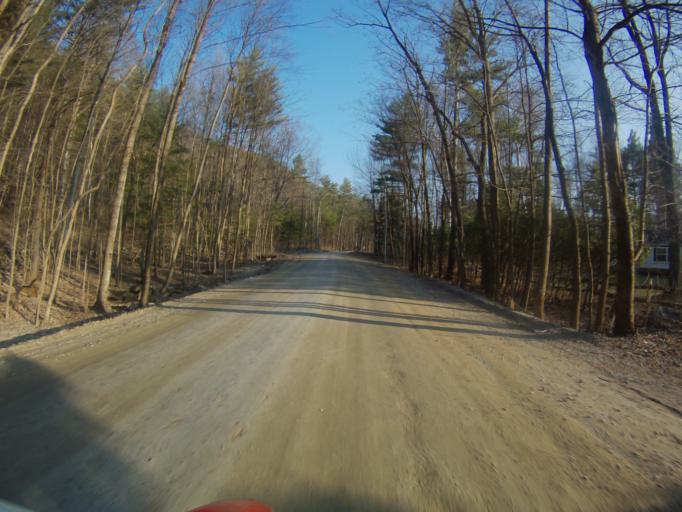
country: US
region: Vermont
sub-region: Addison County
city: Bristol
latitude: 44.1089
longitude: -73.0765
